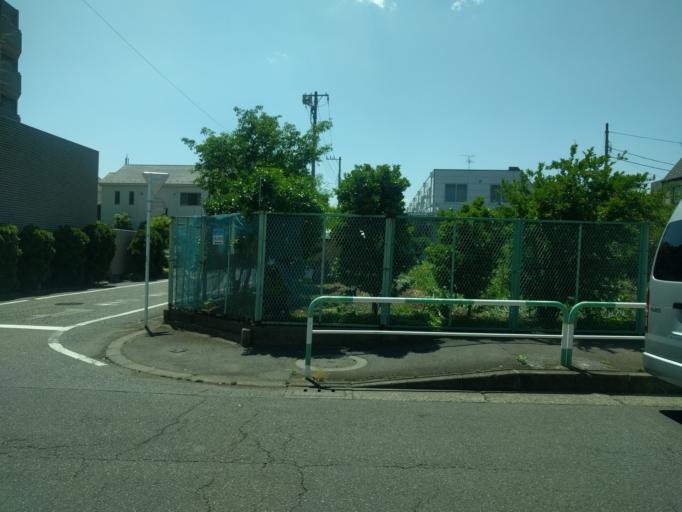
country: JP
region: Tokyo
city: Mitaka-shi
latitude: 35.6602
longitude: 139.6243
